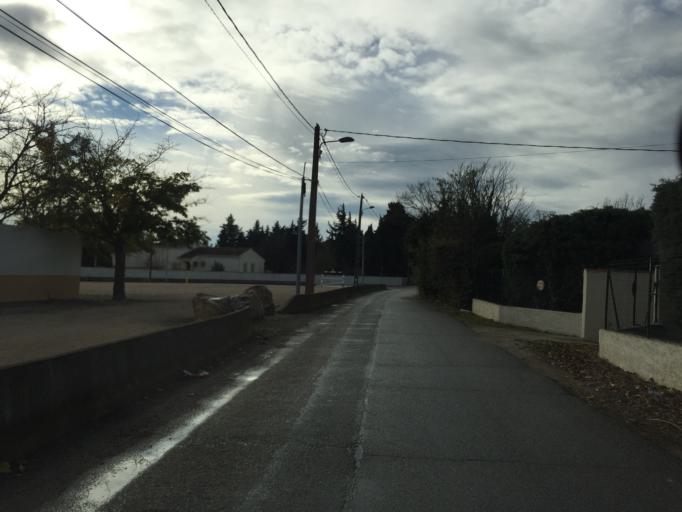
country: FR
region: Provence-Alpes-Cote d'Azur
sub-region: Departement du Vaucluse
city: Vedene
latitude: 43.9939
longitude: 4.8895
